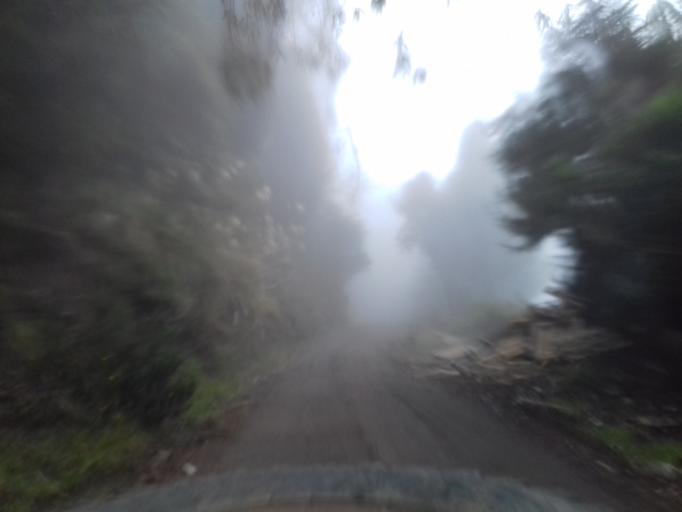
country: CO
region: Tolima
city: Murillo
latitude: 4.9039
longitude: -75.2506
